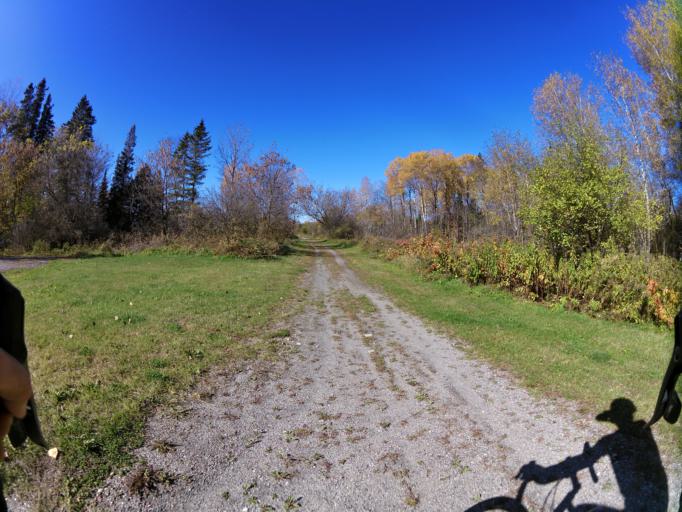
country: CA
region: Quebec
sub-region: Outaouais
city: Wakefield
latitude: 45.8115
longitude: -75.9538
